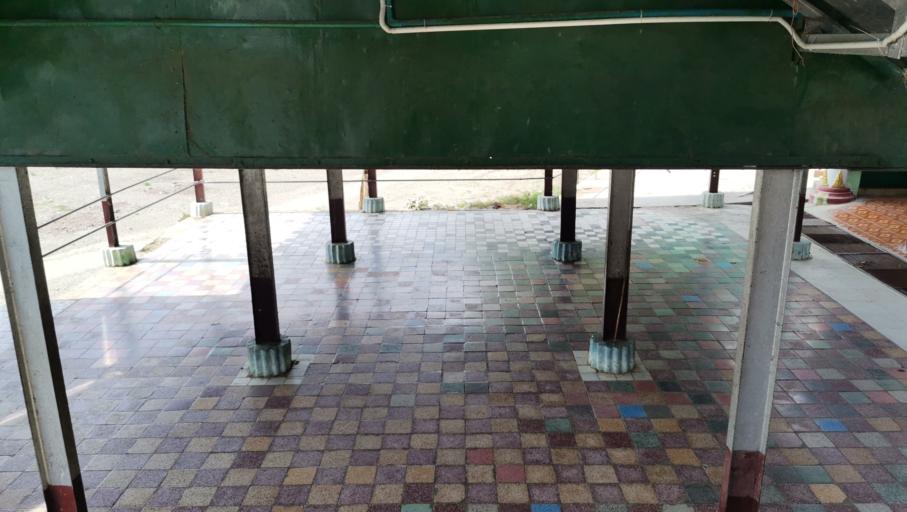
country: MM
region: Magway
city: Minbu
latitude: 20.1020
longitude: 94.5274
